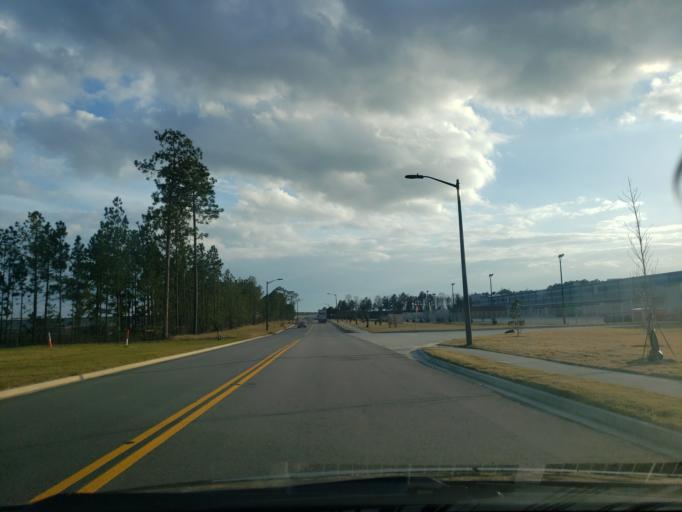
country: US
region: Georgia
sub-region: Chatham County
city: Bloomingdale
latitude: 32.1725
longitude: -81.2700
